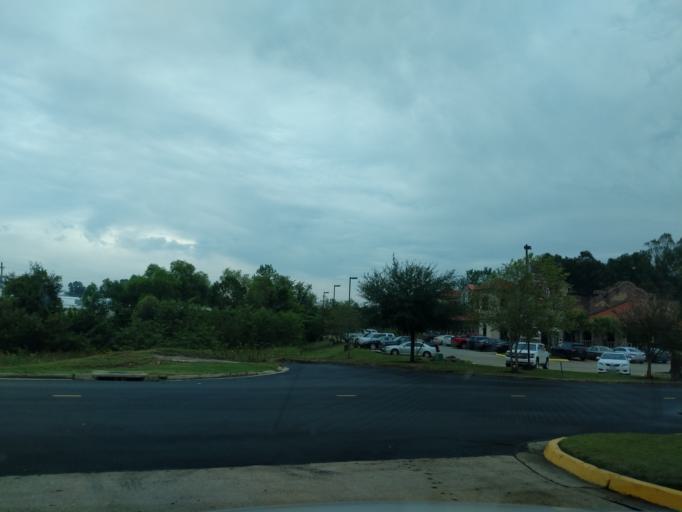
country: US
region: Mississippi
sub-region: Warren County
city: Vicksburg
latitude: 32.3192
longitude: -90.8732
